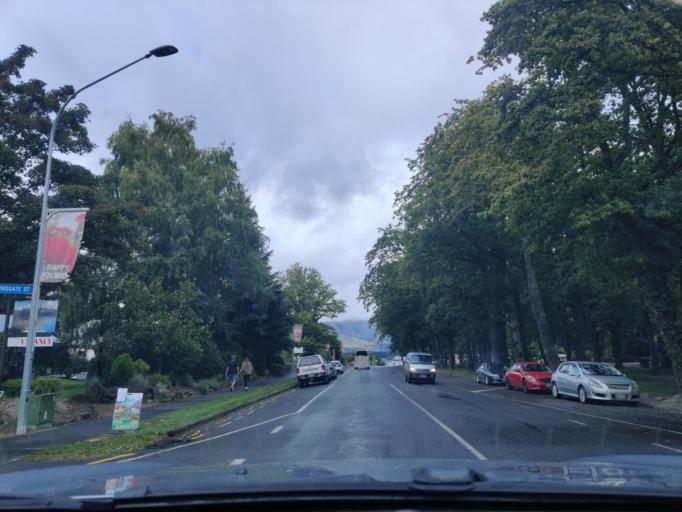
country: NZ
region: Canterbury
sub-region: Hurunui District
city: Amberley
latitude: -42.5239
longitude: 172.8295
